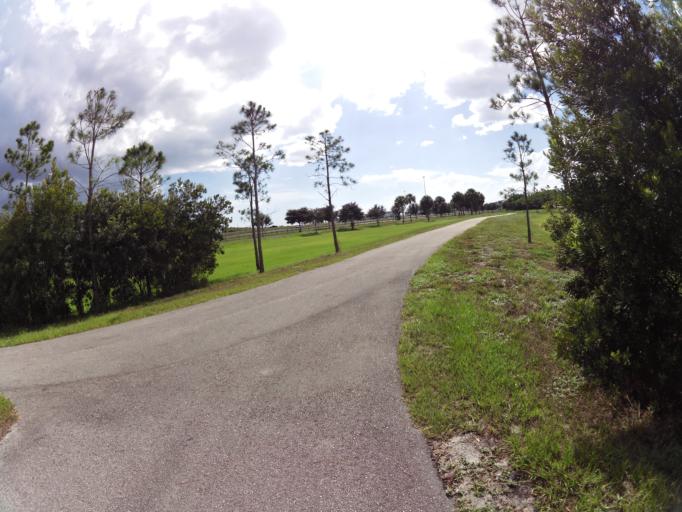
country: US
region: Florida
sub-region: Broward County
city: Southwest Ranches
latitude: 26.0652
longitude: -80.3499
